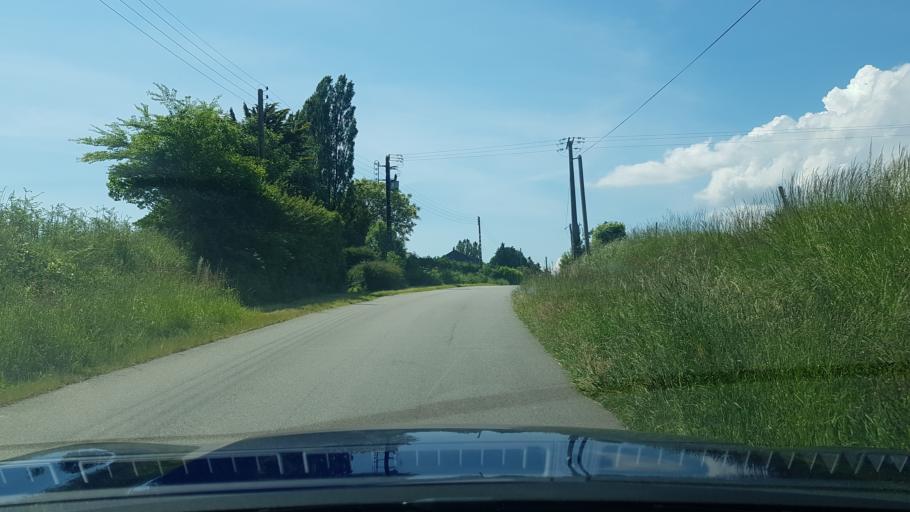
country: FR
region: Brittany
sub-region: Departement du Finistere
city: Clohars-Carnoet
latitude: 47.7877
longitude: -3.5566
